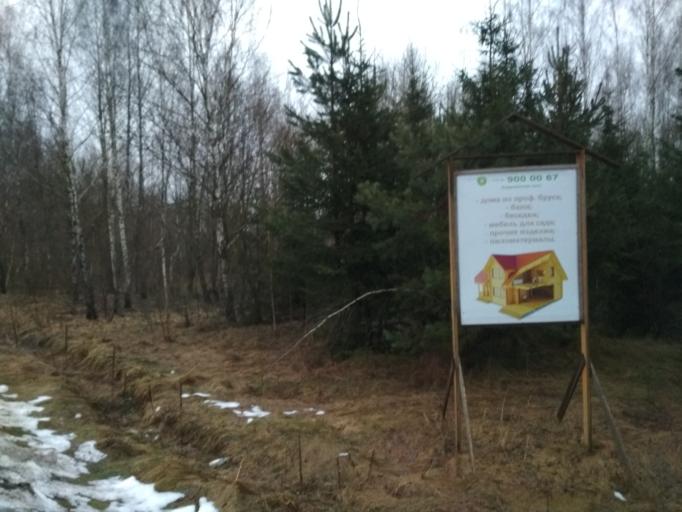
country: BY
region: Minsk
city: Mar''ina Horka
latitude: 53.4913
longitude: 28.1650
